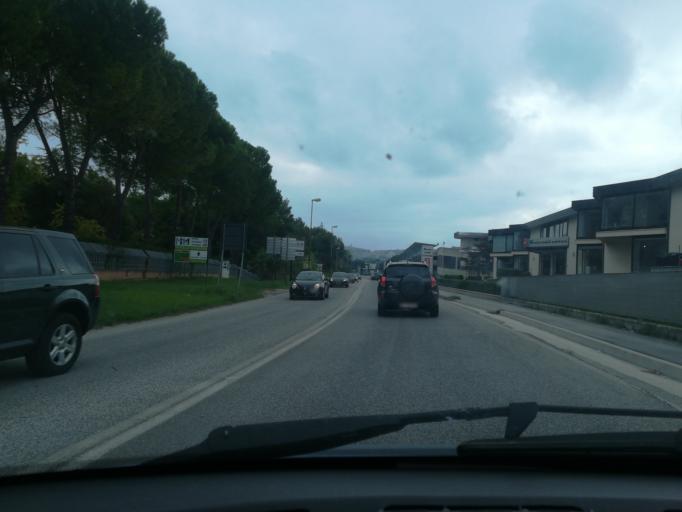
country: IT
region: The Marches
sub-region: Provincia di Macerata
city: Zona Industriale
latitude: 43.2686
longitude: 13.4858
